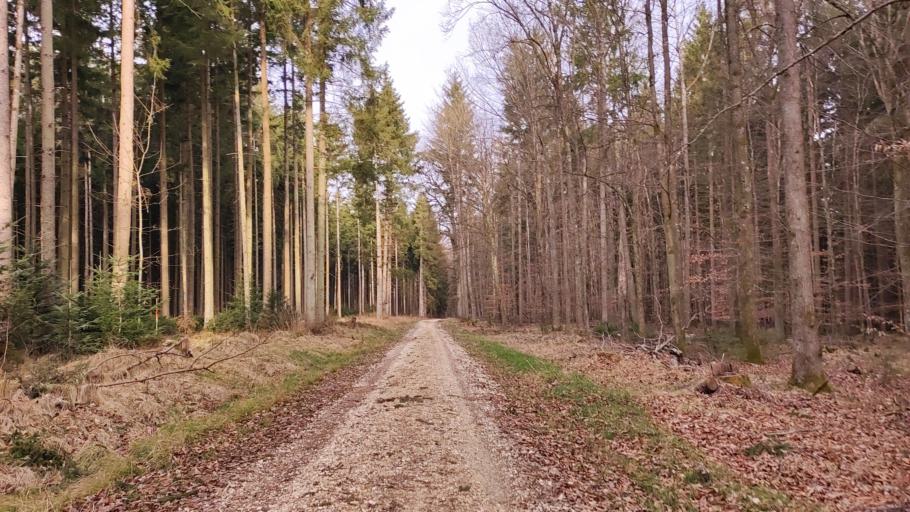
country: DE
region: Bavaria
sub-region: Swabia
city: Zusmarshausen
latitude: 48.4293
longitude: 10.6279
